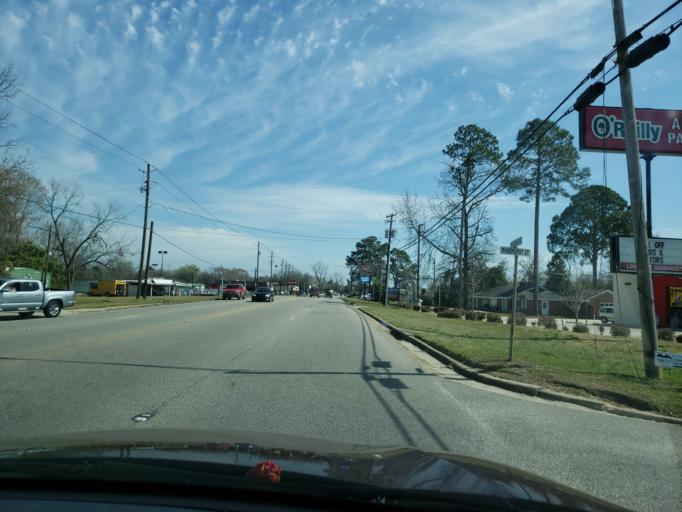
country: US
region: Alabama
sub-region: Elmore County
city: Tallassee
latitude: 32.5515
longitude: -85.9196
